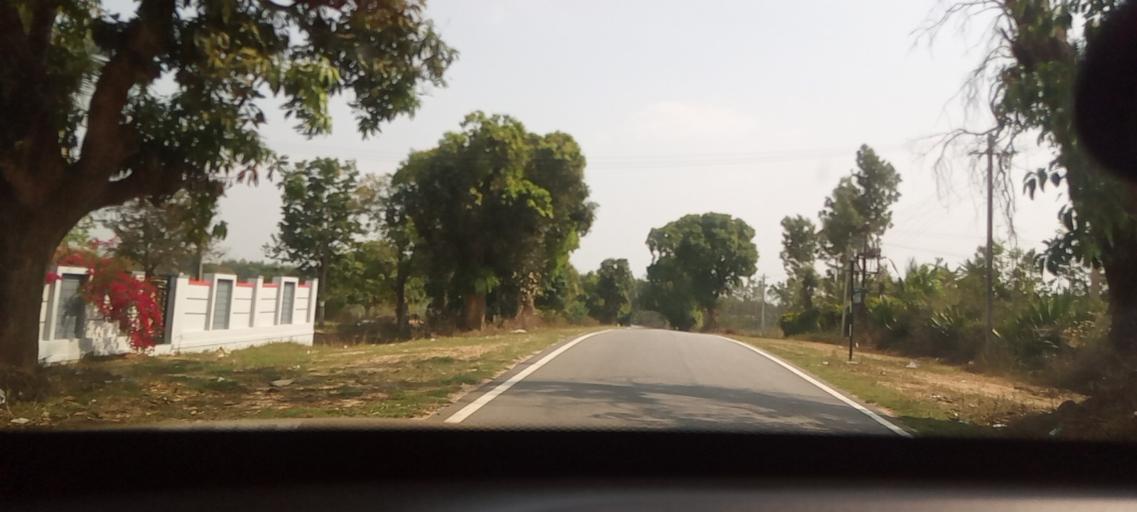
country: IN
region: Karnataka
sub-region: Hassan
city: Belur
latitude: 13.1831
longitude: 75.8020
